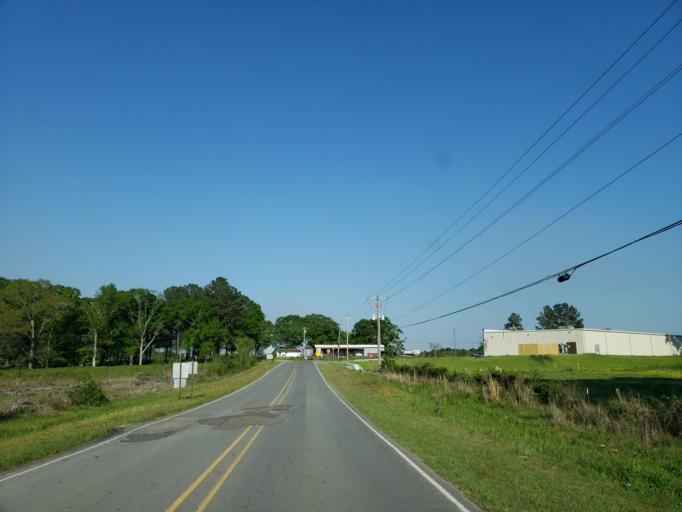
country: US
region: Mississippi
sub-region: Perry County
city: Richton
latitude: 31.4824
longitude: -89.0181
